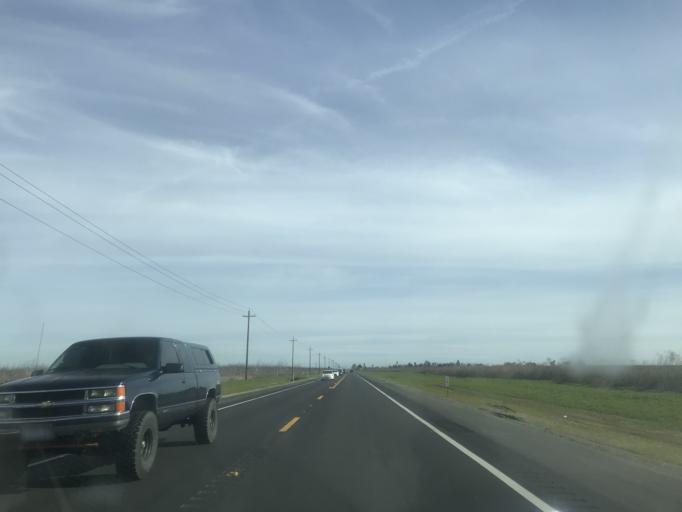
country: US
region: California
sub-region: Yolo County
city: Cottonwood
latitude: 38.6846
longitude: -121.9866
